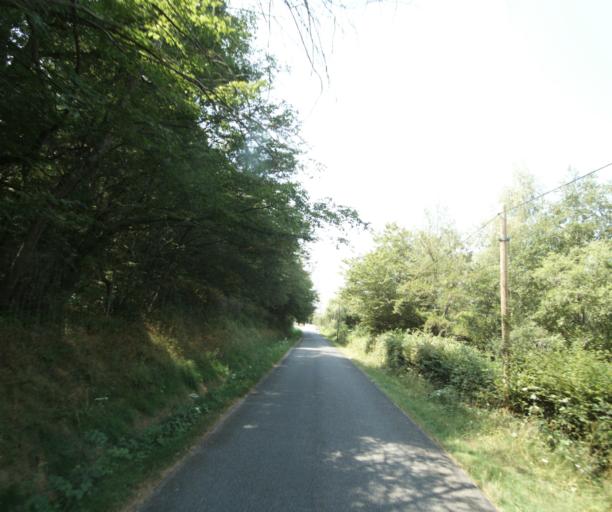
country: FR
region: Bourgogne
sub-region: Departement de Saone-et-Loire
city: Gueugnon
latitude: 46.6127
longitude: 4.0374
